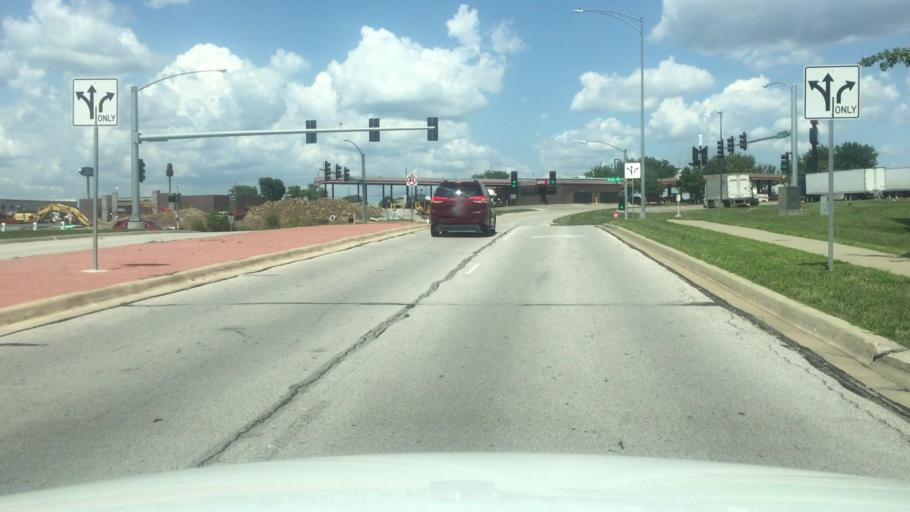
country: US
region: Missouri
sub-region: Platte County
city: Platte City
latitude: 39.3534
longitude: -94.7674
